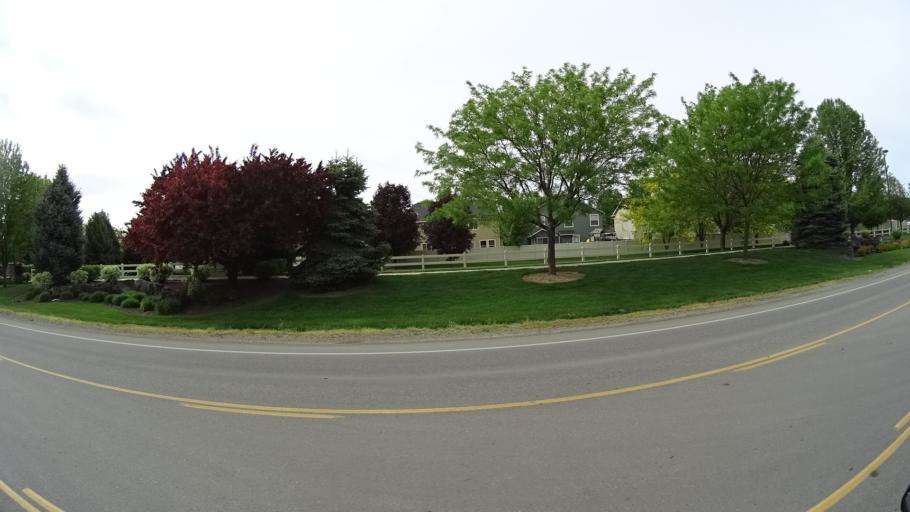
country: US
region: Idaho
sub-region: Ada County
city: Garden City
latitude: 43.5465
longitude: -116.3071
